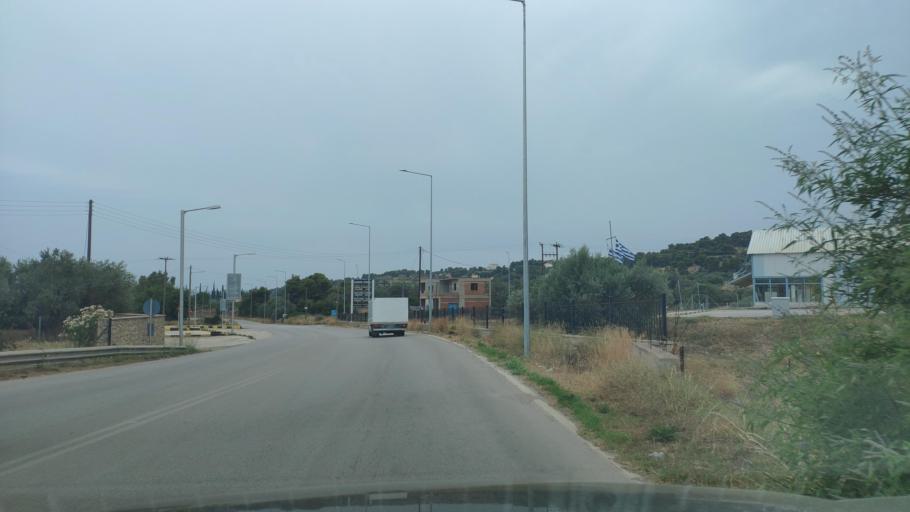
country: GR
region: Peloponnese
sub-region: Nomos Argolidos
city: Kranidi
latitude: 37.3520
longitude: 23.1577
